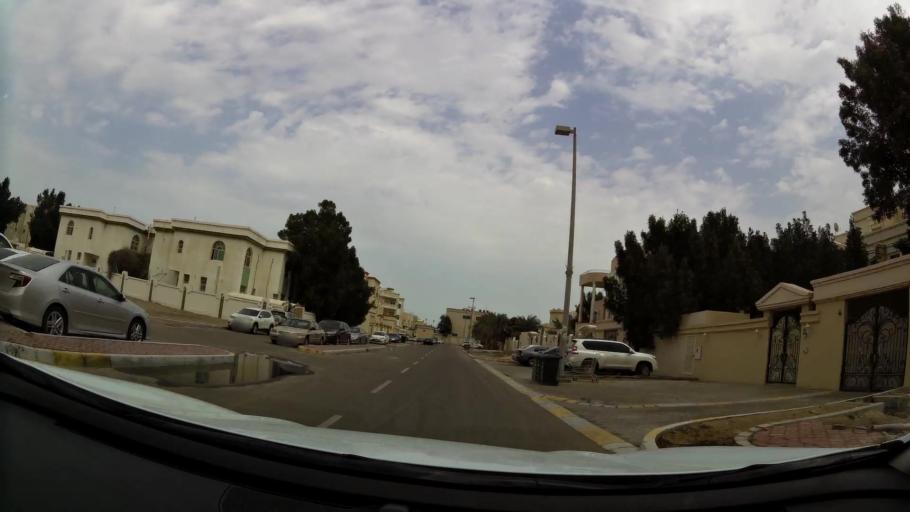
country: AE
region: Abu Dhabi
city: Abu Dhabi
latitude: 24.4378
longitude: 54.4419
